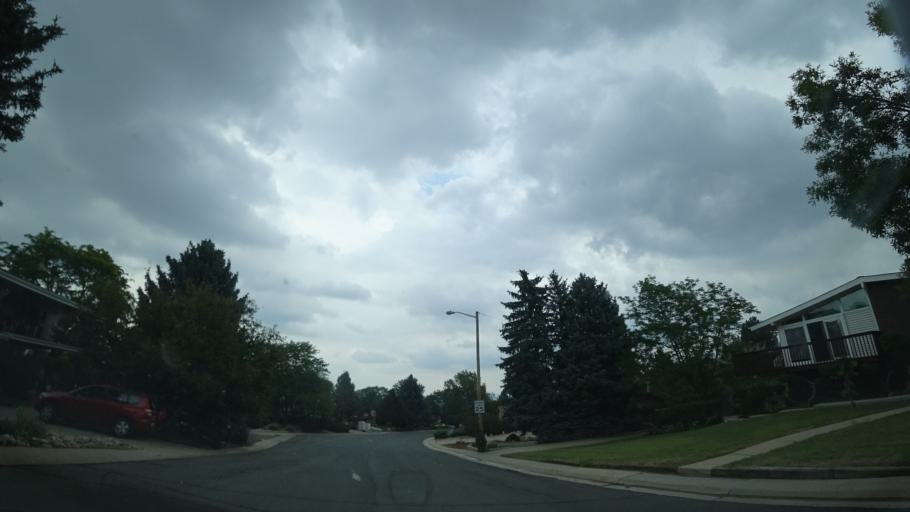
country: US
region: Colorado
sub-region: Jefferson County
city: West Pleasant View
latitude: 39.7021
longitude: -105.1520
